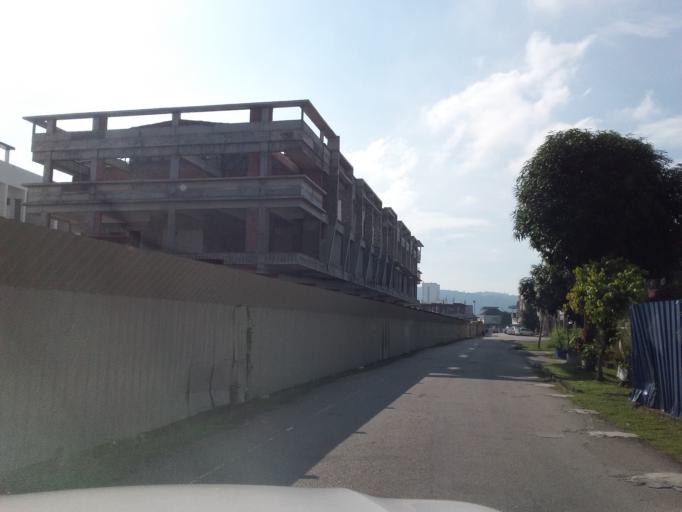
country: MY
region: Johor
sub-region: Daerah Batu Pahat
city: Batu Pahat
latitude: 1.8588
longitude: 102.9282
